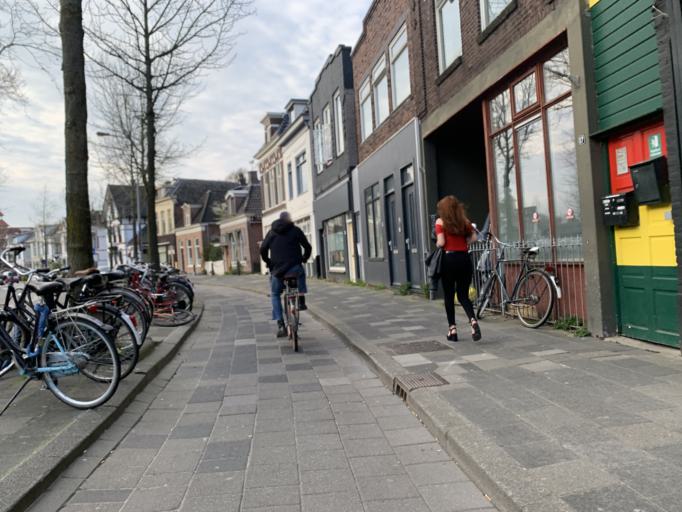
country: NL
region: Groningen
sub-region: Gemeente Groningen
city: Korrewegwijk
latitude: 53.2287
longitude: 6.5597
